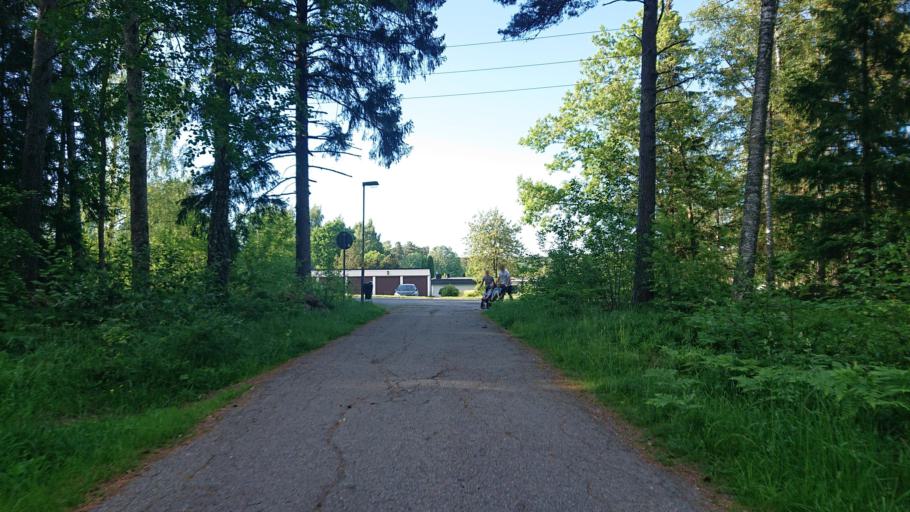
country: SE
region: Stockholm
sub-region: Osterakers Kommun
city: Akersberga
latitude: 59.5069
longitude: 18.3046
